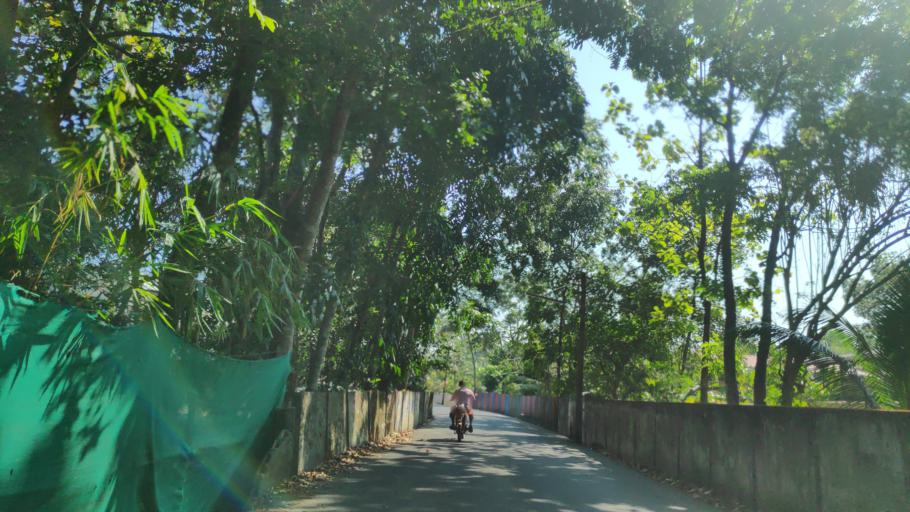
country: IN
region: Kerala
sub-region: Alappuzha
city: Alleppey
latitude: 9.5723
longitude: 76.3168
